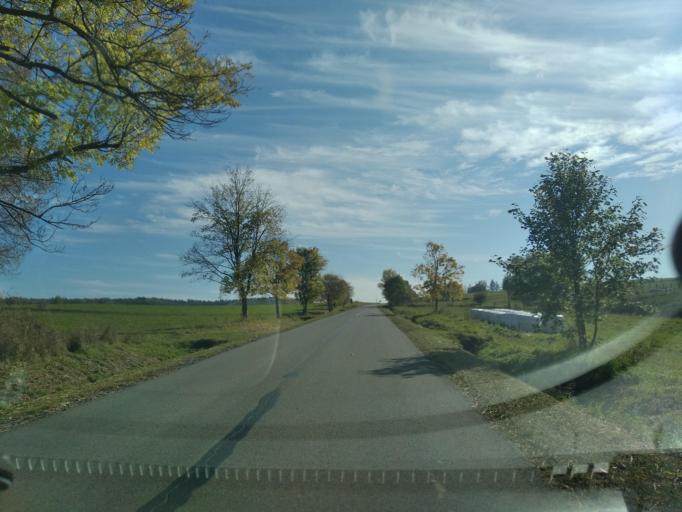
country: PL
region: Subcarpathian Voivodeship
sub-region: Powiat sanocki
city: Komancza
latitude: 49.3856
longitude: 21.9931
